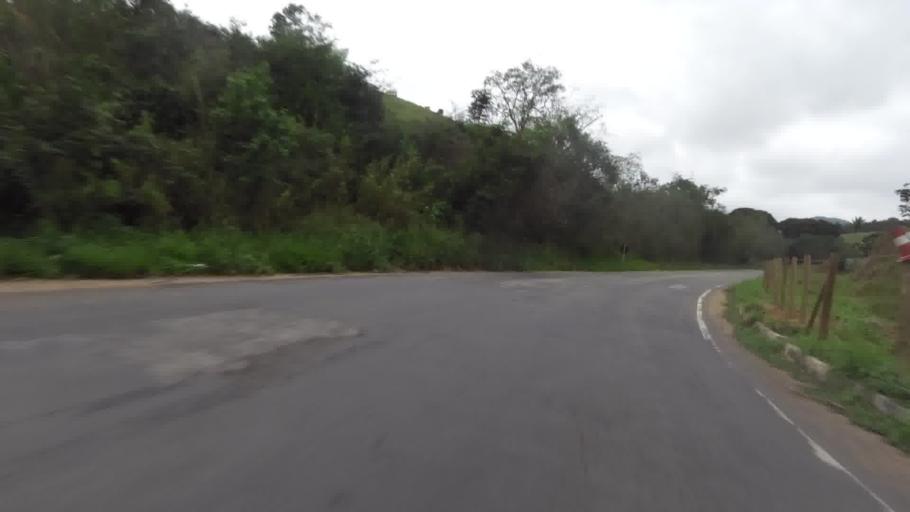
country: BR
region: Espirito Santo
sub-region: Alfredo Chaves
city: Alfredo Chaves
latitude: -20.6688
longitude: -40.7060
